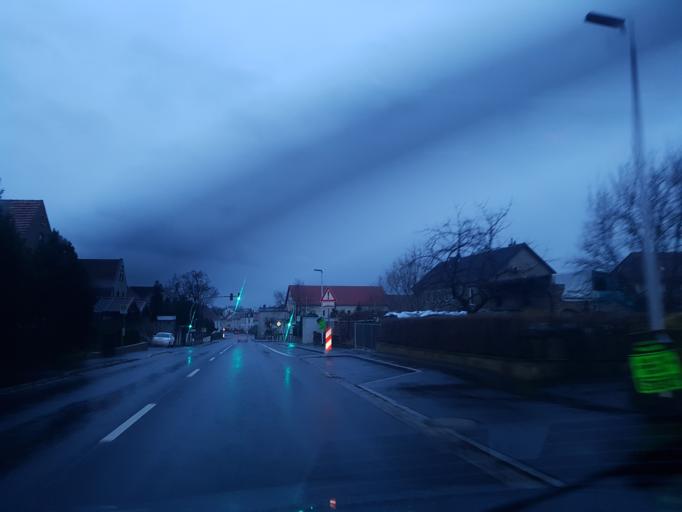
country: DE
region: Saxony
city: Priestewitz
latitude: 51.2551
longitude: 13.5093
